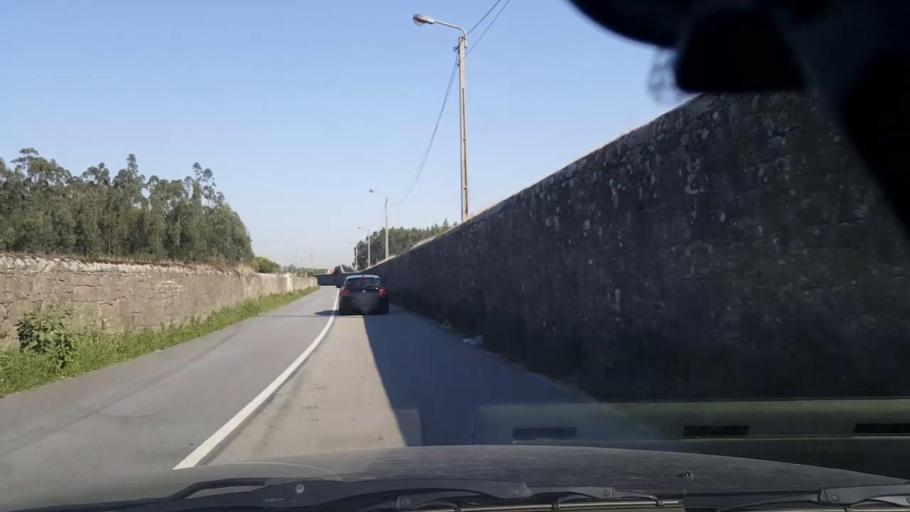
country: PT
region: Porto
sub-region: Vila do Conde
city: Arvore
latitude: 41.3295
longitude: -8.6802
